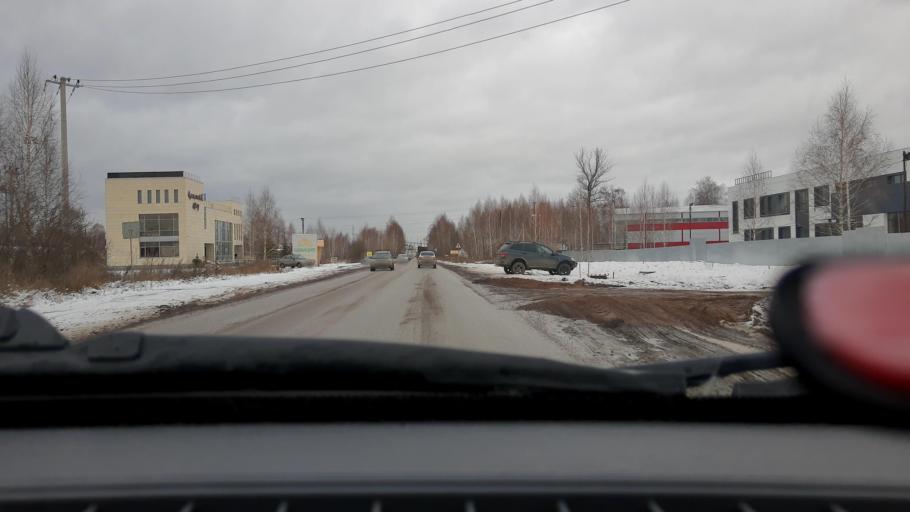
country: RU
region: Bashkortostan
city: Ufa
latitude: 54.6652
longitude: 56.0762
